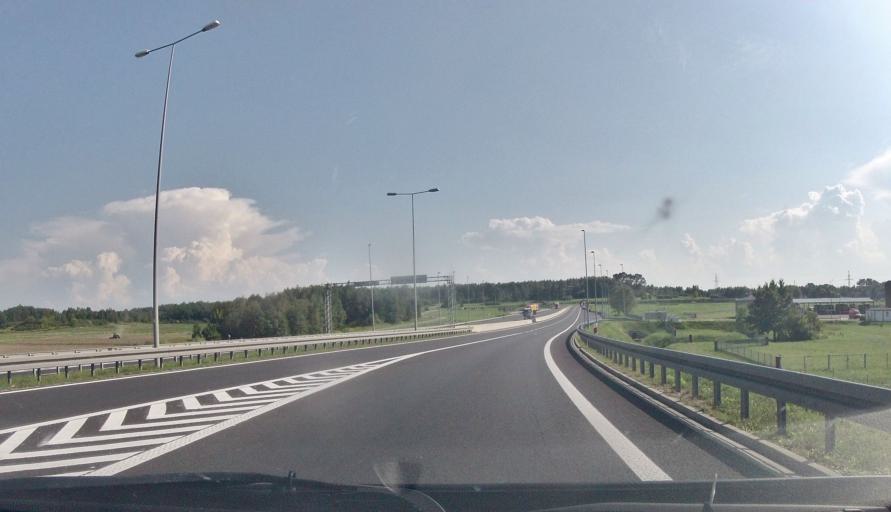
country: PL
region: Lesser Poland Voivodeship
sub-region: Powiat tarnowski
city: Lisia Gora
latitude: 50.0528
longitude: 21.0140
